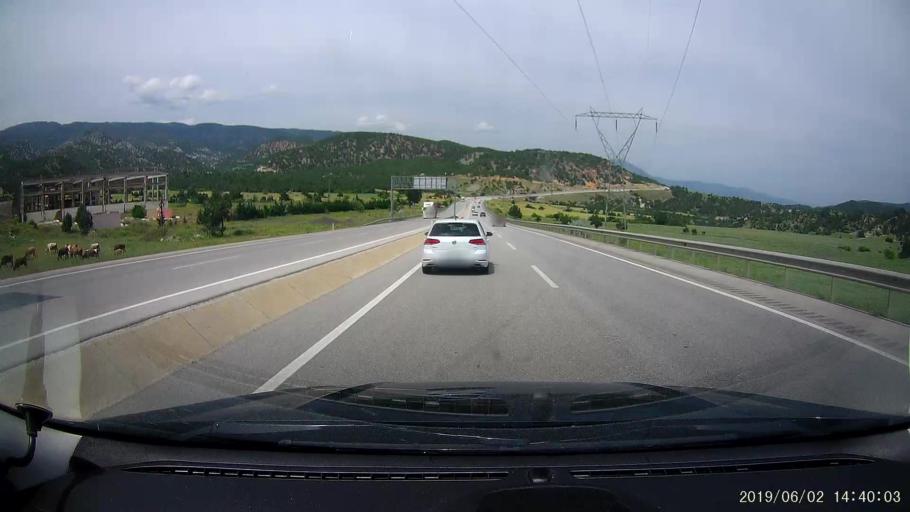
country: TR
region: Corum
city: Hacihamza
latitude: 41.0773
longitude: 34.3122
